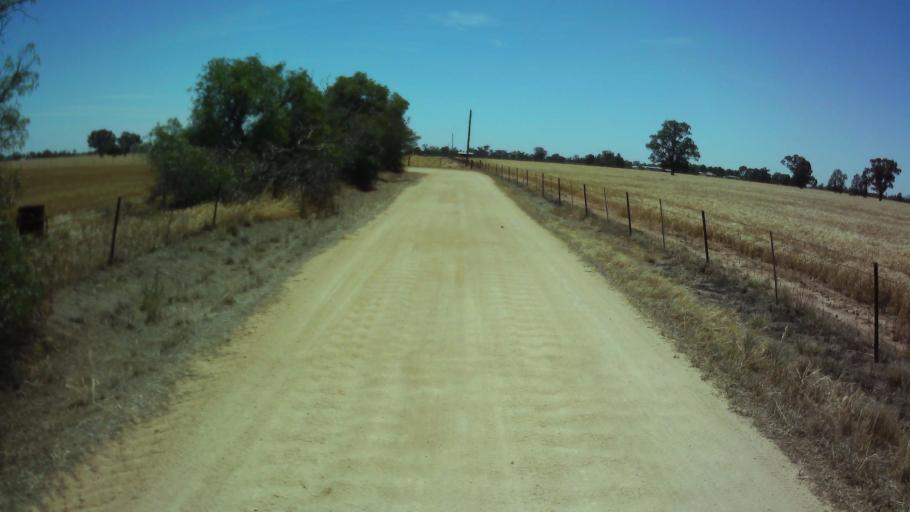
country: AU
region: New South Wales
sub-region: Weddin
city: Grenfell
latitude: -34.0561
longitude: 147.7755
